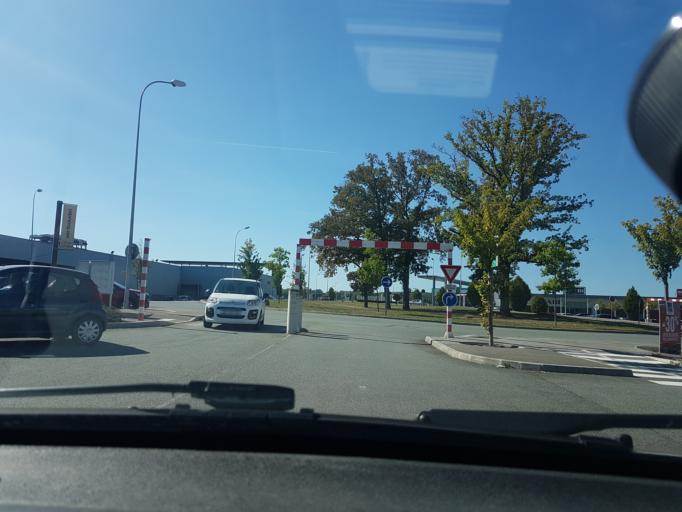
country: FR
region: Franche-Comte
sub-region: Territoire de Belfort
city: Chevremont
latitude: 47.6416
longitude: 6.9205
